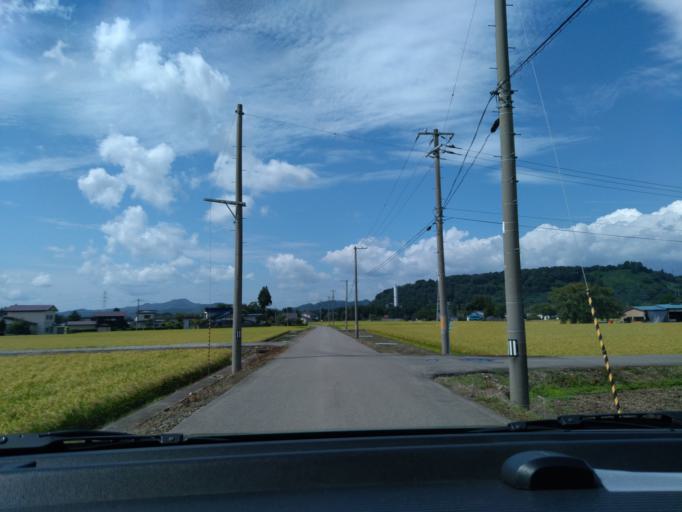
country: JP
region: Akita
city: Kakunodatemachi
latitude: 39.5775
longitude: 140.5897
